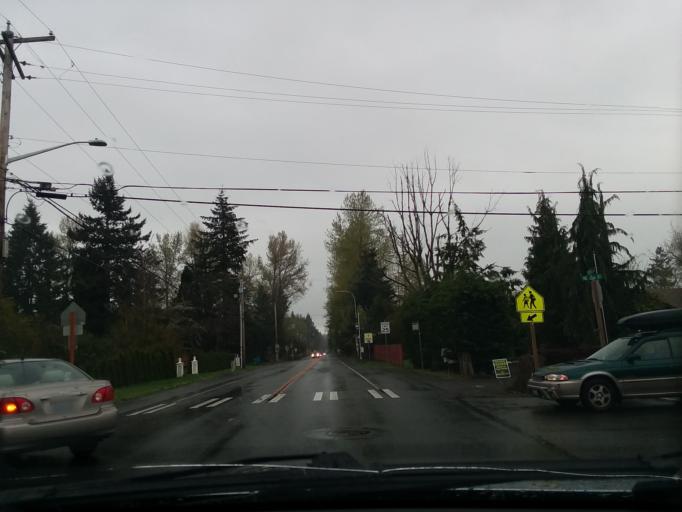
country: US
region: Washington
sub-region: King County
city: East Renton Highlands
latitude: 47.4850
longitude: -122.1483
